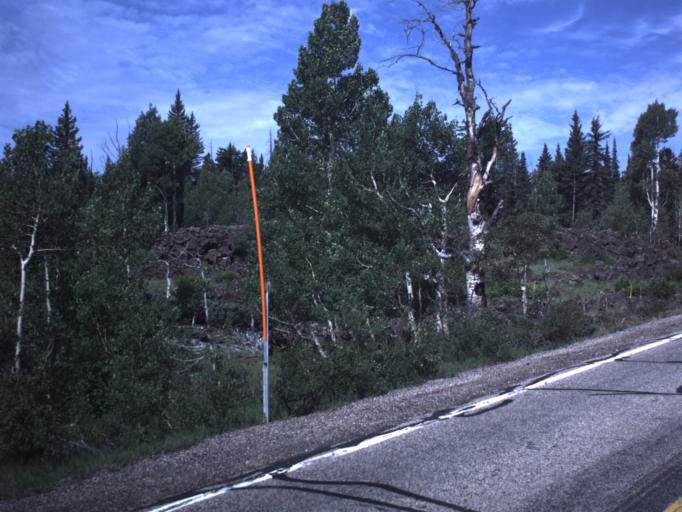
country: US
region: Utah
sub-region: Iron County
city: Parowan
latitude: 37.5187
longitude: -112.7038
